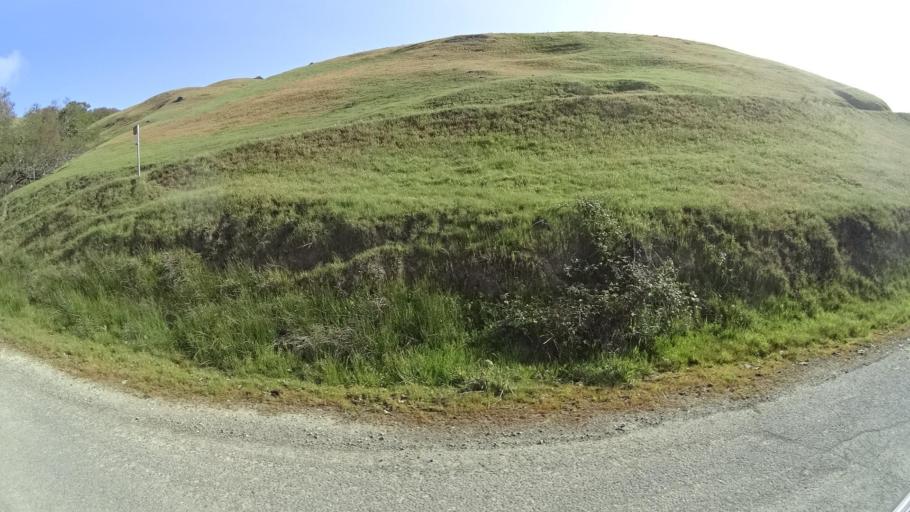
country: US
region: California
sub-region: Humboldt County
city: Hydesville
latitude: 40.6390
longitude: -123.8993
